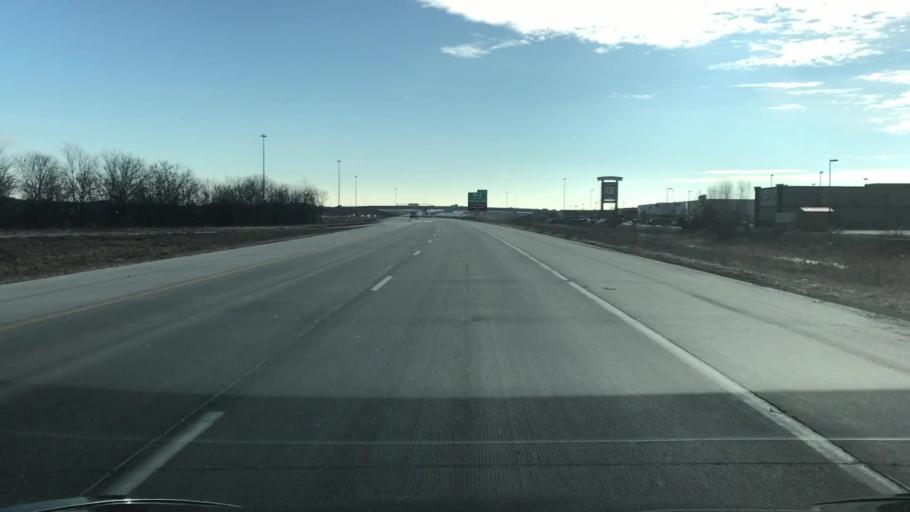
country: US
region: Iowa
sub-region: Pottawattamie County
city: Council Bluffs
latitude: 41.2259
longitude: -95.8381
